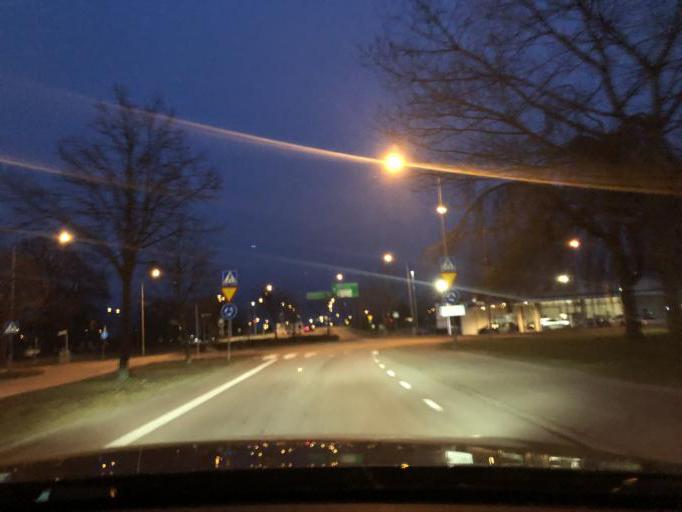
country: SE
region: Kalmar
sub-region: Kalmar Kommun
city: Kalmar
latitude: 56.6755
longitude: 16.3211
